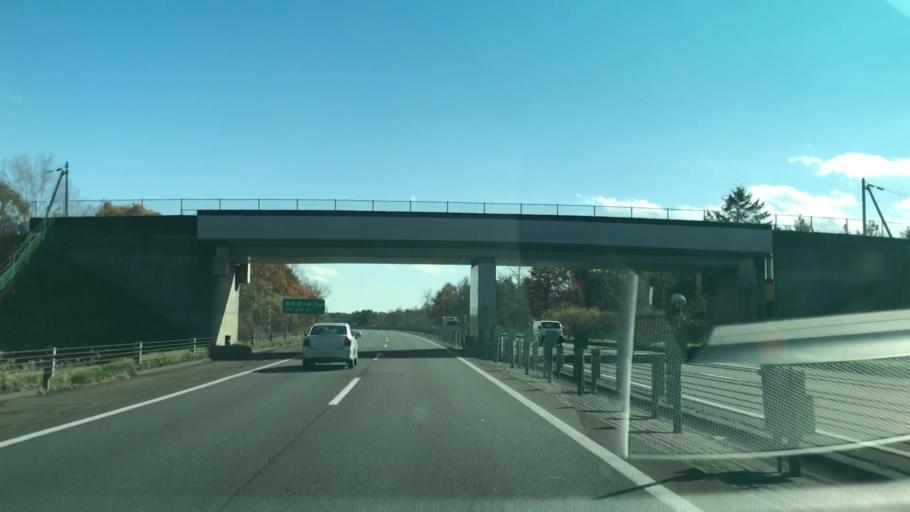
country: JP
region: Hokkaido
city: Chitose
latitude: 42.8574
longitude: 141.5619
